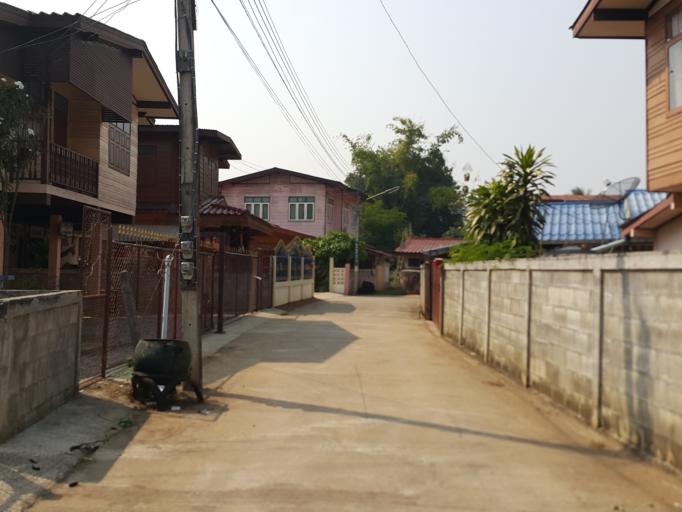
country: TH
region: Sukhothai
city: Thung Saliam
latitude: 17.3269
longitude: 99.5326
